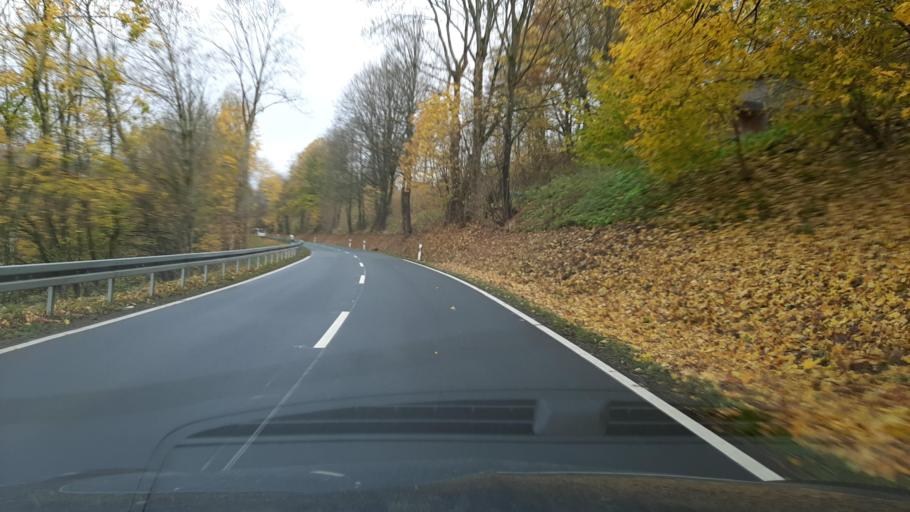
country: DE
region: North Rhine-Westphalia
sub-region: Regierungsbezirk Arnsberg
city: Winterberg
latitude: 51.2574
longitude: 8.4726
